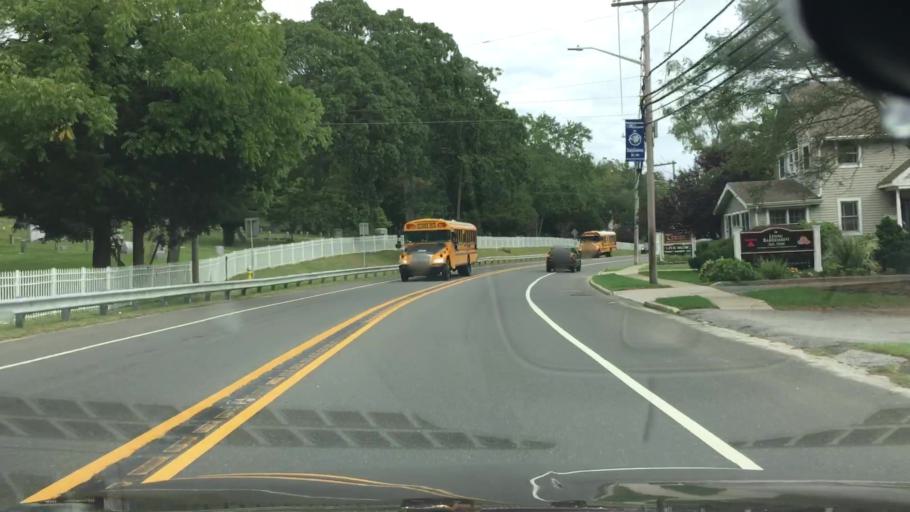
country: US
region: New York
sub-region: Suffolk County
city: Village of the Branch
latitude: 40.8579
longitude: -73.1864
